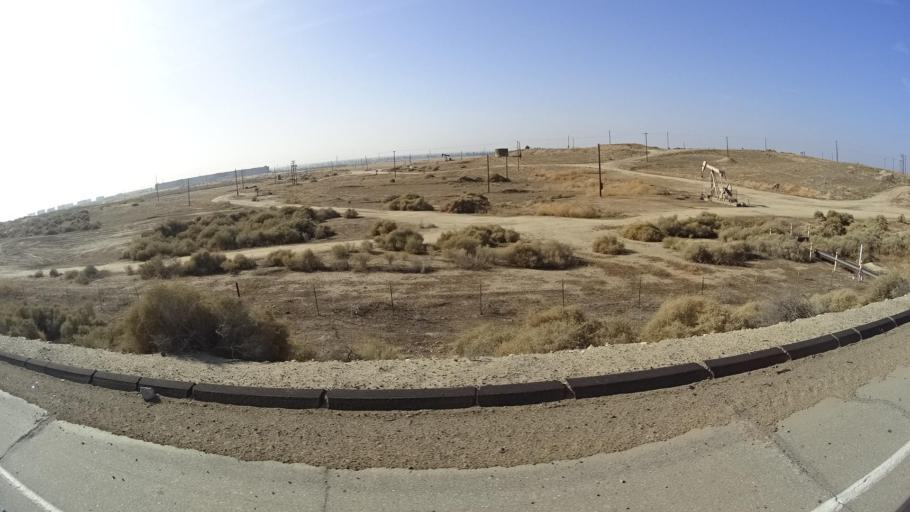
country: US
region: California
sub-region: Kern County
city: Oildale
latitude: 35.4598
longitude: -119.0488
